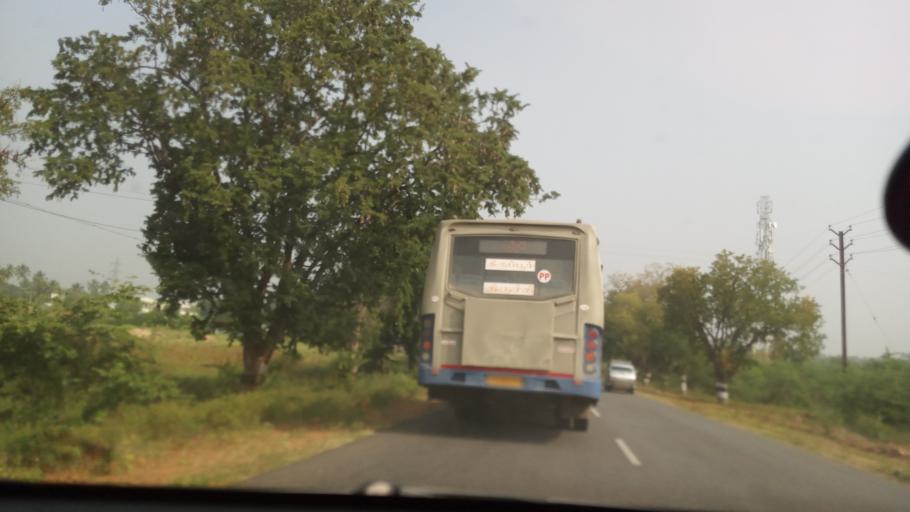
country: IN
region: Tamil Nadu
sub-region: Erode
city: Punjai Puliyampatti
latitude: 11.4180
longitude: 77.1946
